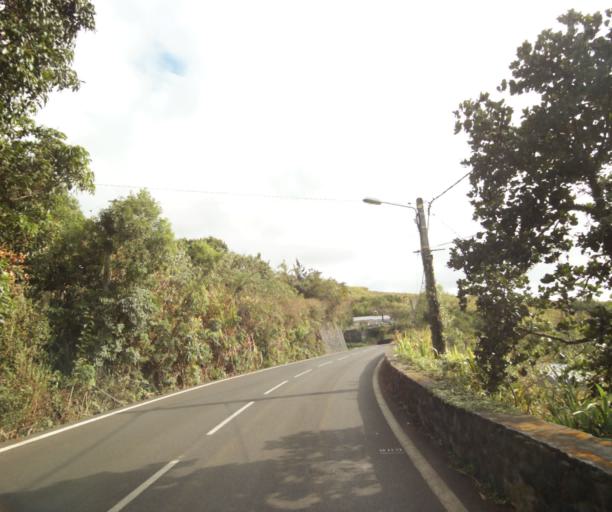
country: RE
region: Reunion
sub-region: Reunion
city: Saint-Paul
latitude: -21.0181
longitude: 55.3168
